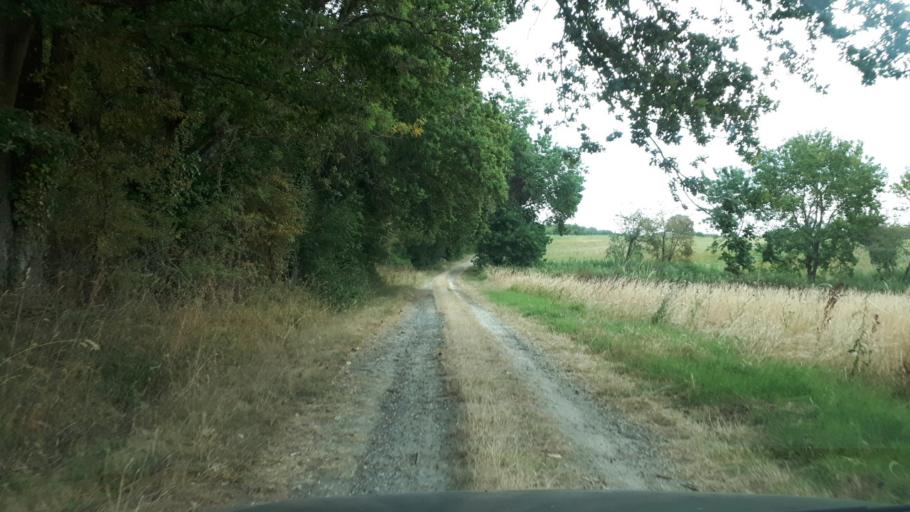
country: FR
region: Centre
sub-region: Departement du Loir-et-Cher
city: Saint-Romain-sur-Cher
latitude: 47.3517
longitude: 1.3970
